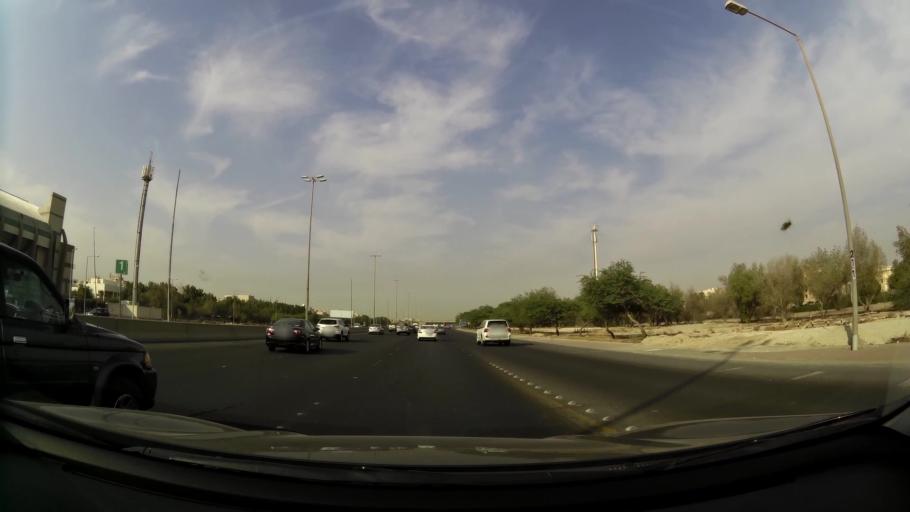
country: KW
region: Mubarak al Kabir
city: Sabah as Salim
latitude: 29.2662
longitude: 48.0740
